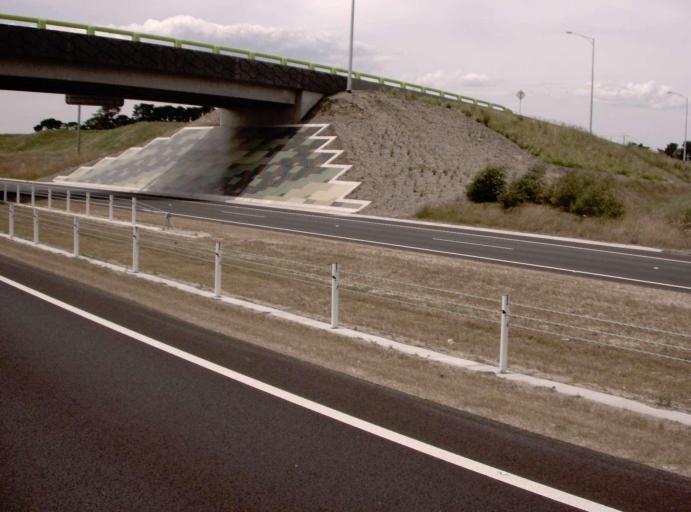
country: AU
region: Victoria
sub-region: Mornington Peninsula
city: Moorooduc
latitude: -38.2332
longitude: 145.1250
